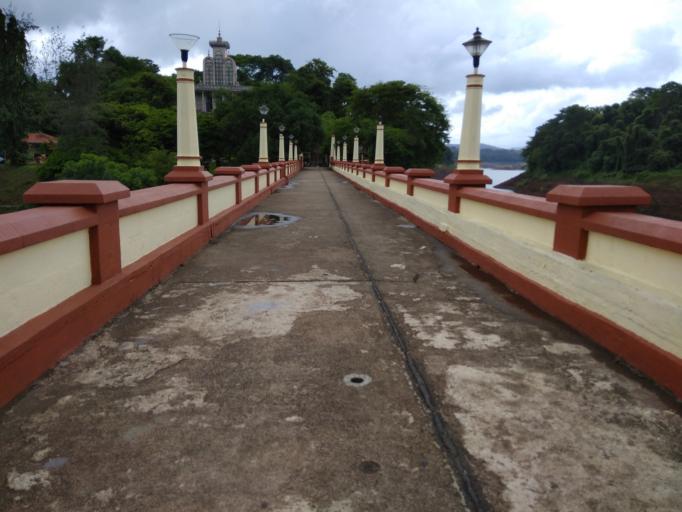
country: IN
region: Kerala
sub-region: Thrissur District
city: Trichur
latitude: 10.5301
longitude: 76.3703
